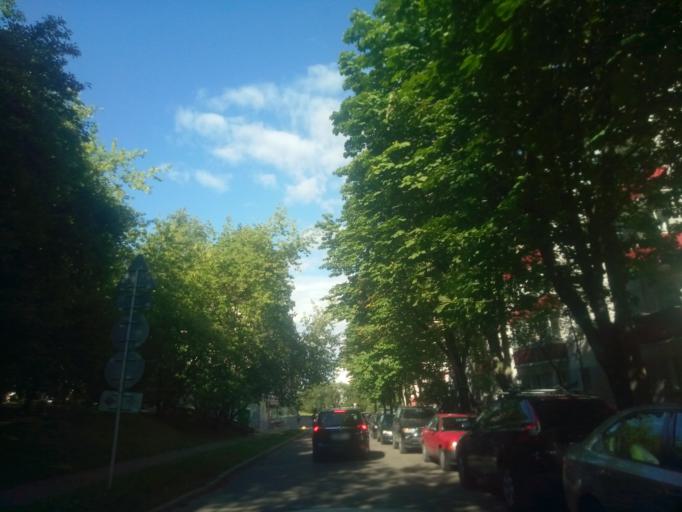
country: BY
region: Minsk
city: Minsk
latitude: 53.8982
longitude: 27.5234
